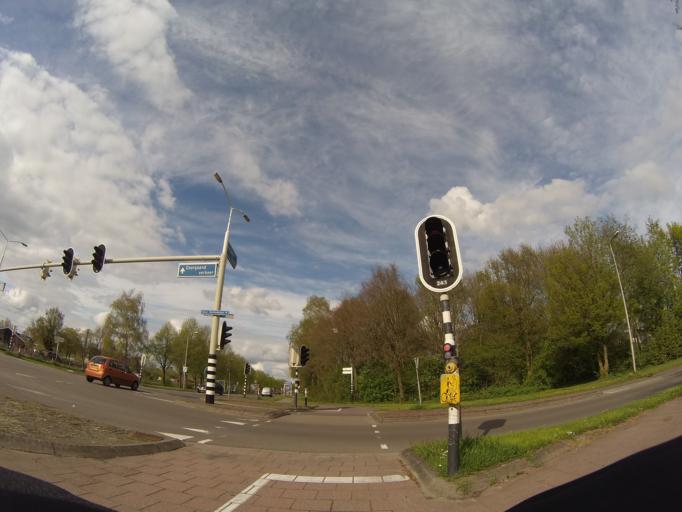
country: NL
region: Drenthe
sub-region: Gemeente Coevorden
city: Coevorden
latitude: 52.6729
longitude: 6.7446
